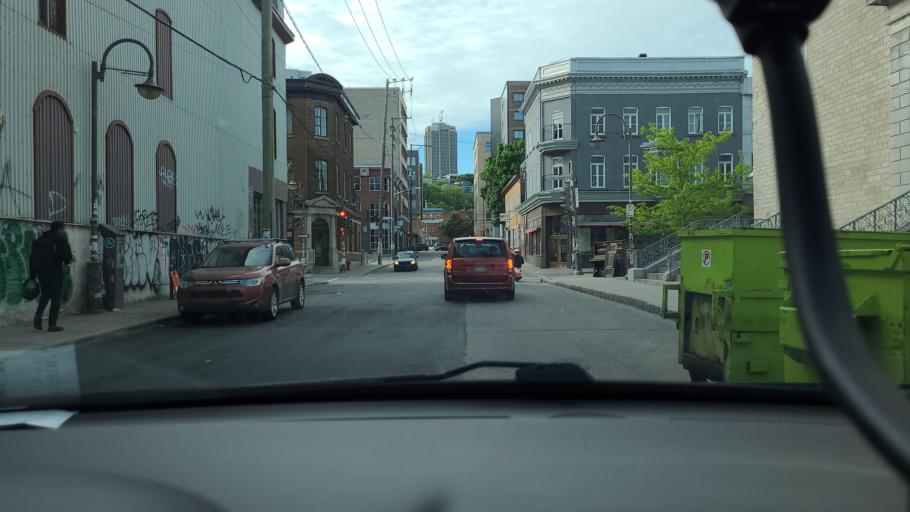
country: CA
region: Quebec
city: Quebec
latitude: 46.8133
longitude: -71.2287
